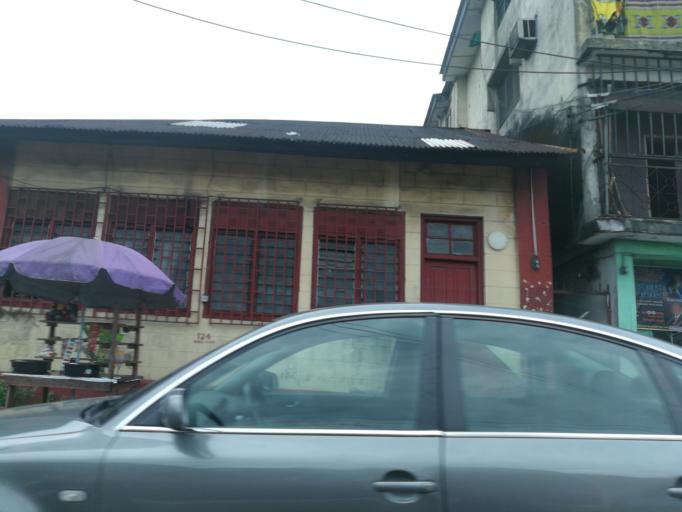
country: NG
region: Rivers
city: Port Harcourt
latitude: 4.7606
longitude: 7.0263
